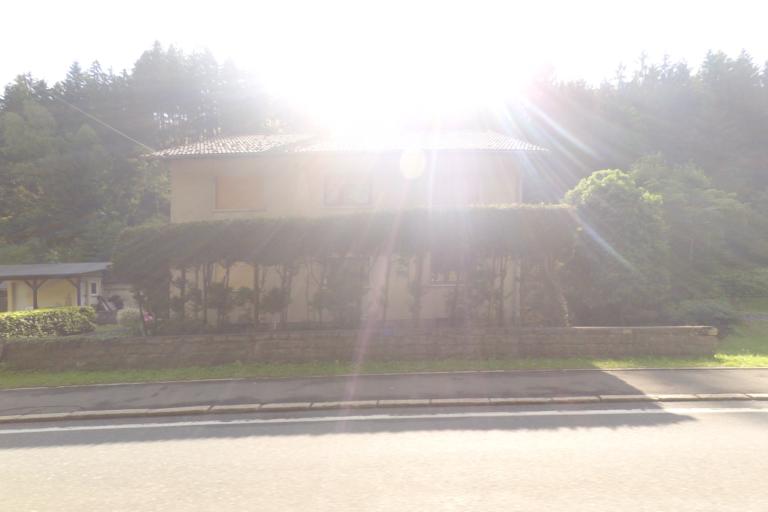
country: DE
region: Bavaria
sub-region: Upper Franconia
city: Ludwigsstadt
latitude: 50.5030
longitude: 11.3700
